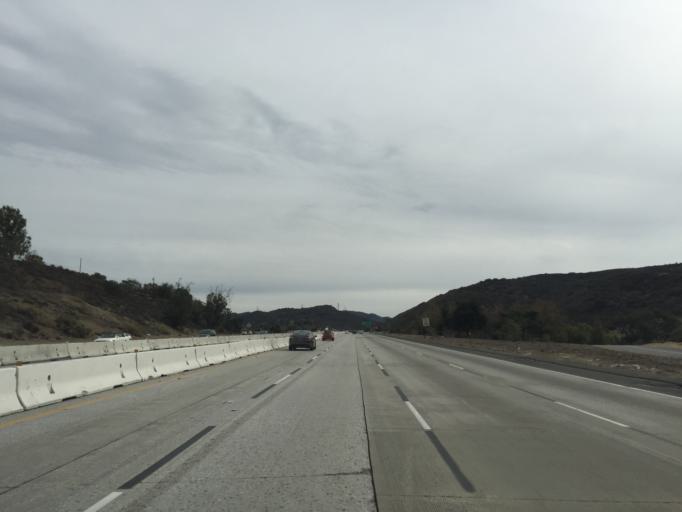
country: US
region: California
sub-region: Los Angeles County
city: Burbank
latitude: 34.2628
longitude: -118.3330
